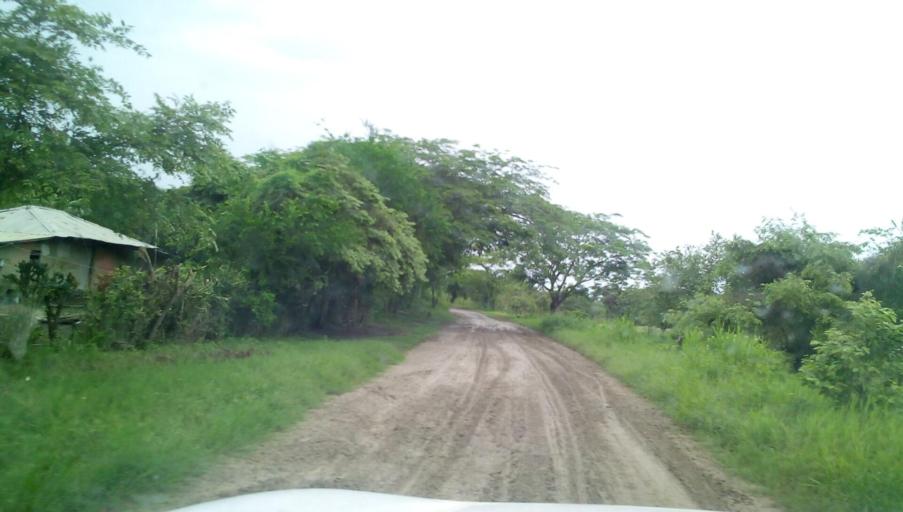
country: MX
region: Veracruz
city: Panuco
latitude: 21.8059
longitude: -98.1058
